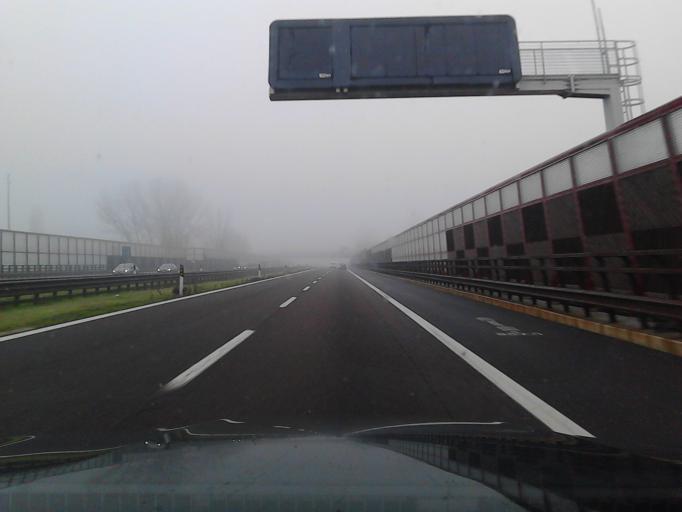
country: IT
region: Emilia-Romagna
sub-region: Provincia di Modena
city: Campogalliano
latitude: 44.7217
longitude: 10.8454
